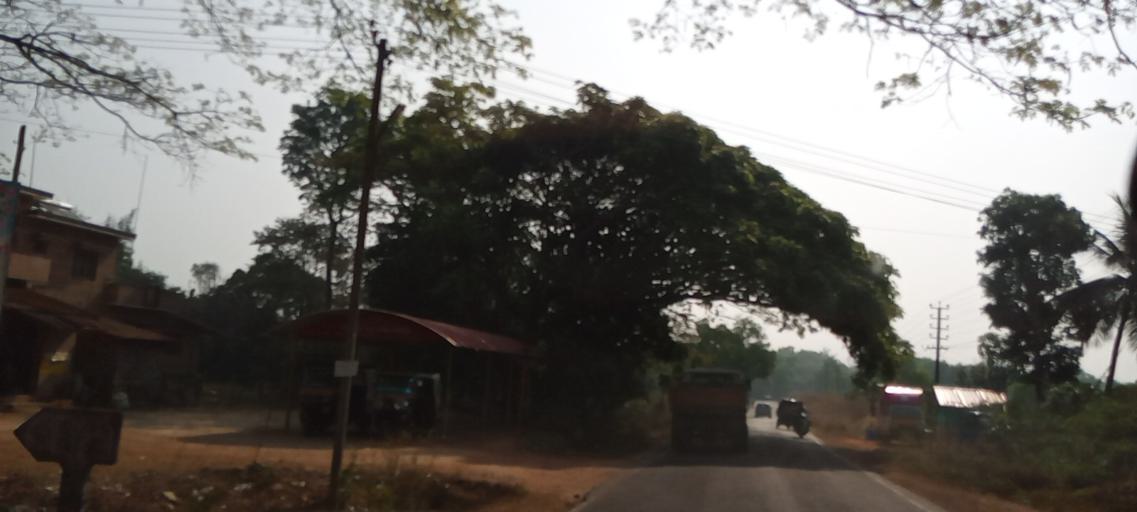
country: IN
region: Karnataka
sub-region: Udupi
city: Coondapoor
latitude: 13.5174
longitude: 74.7628
